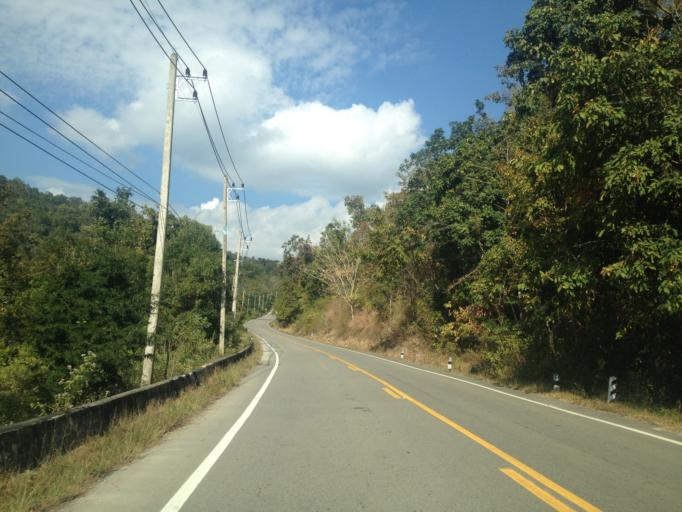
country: TH
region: Mae Hong Son
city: Ban Huai I Huak
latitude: 18.1354
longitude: 98.1776
